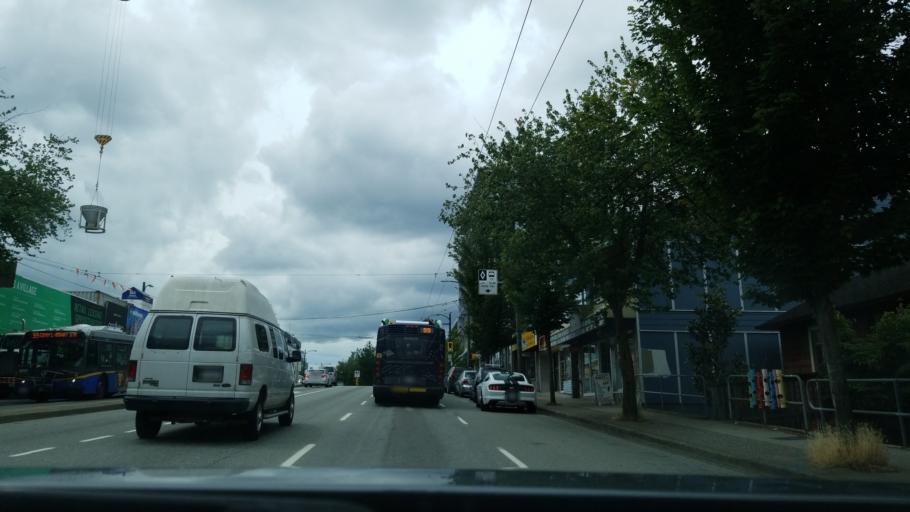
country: CA
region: British Columbia
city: Vancouver
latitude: 49.2625
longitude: -123.0881
